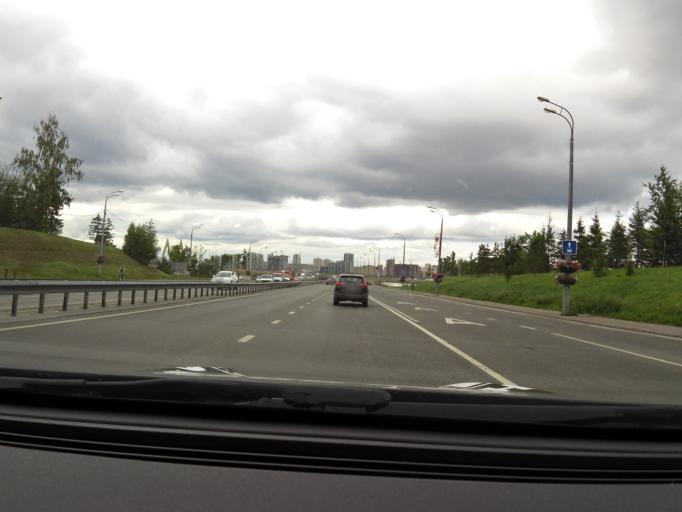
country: RU
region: Tatarstan
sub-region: Gorod Kazan'
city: Kazan
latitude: 55.8012
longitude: 49.1518
